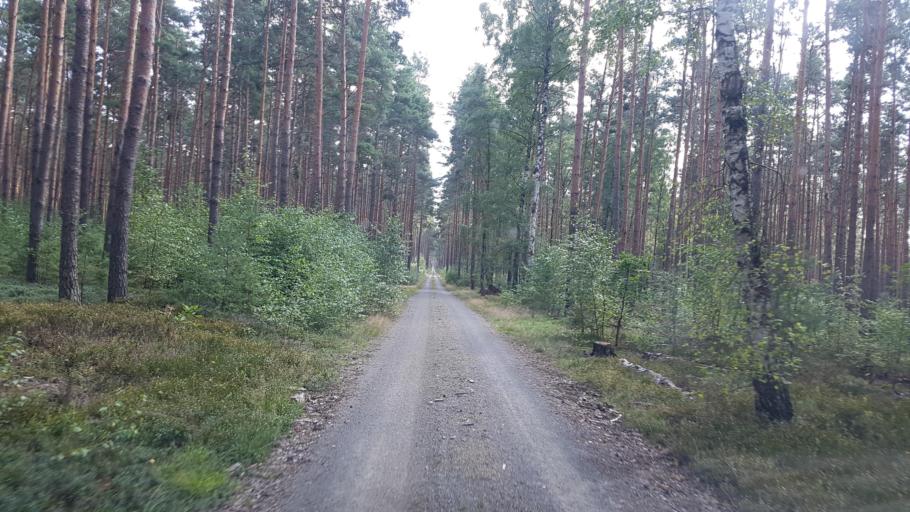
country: DE
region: Brandenburg
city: Hohenbucko
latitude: 51.7773
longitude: 13.5307
